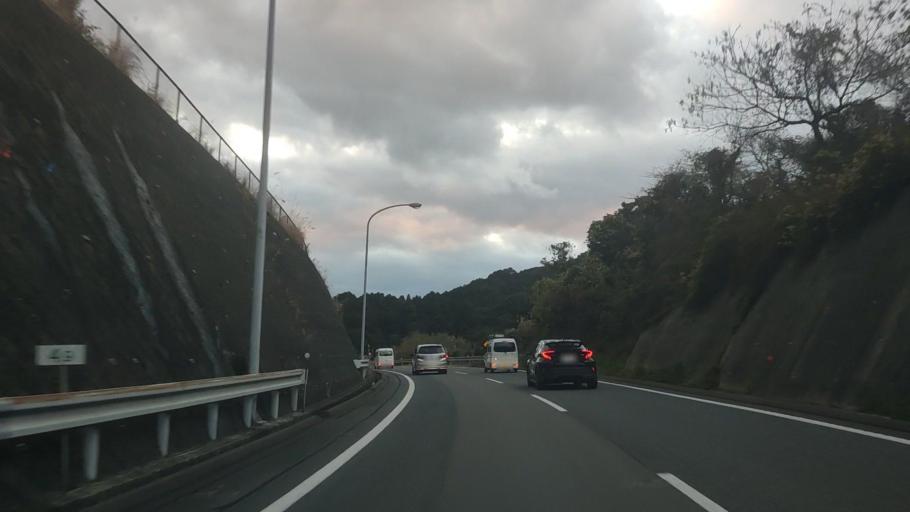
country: JP
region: Nagasaki
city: Obita
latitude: 32.8148
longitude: 129.9261
